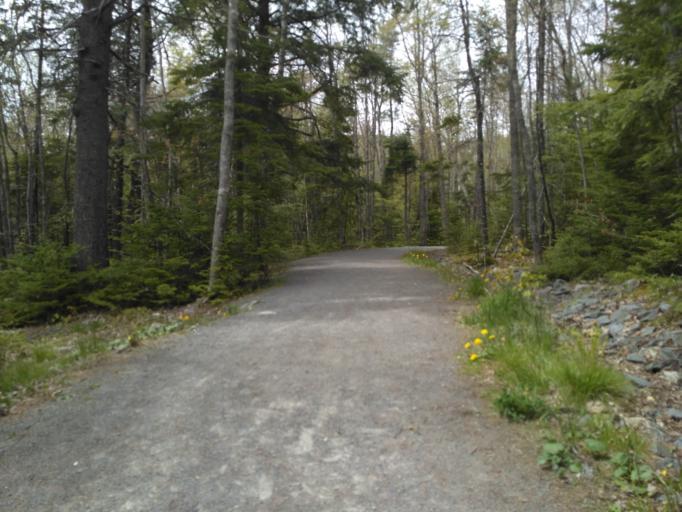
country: CA
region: Nova Scotia
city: Dartmouth
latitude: 44.7683
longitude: -63.6540
